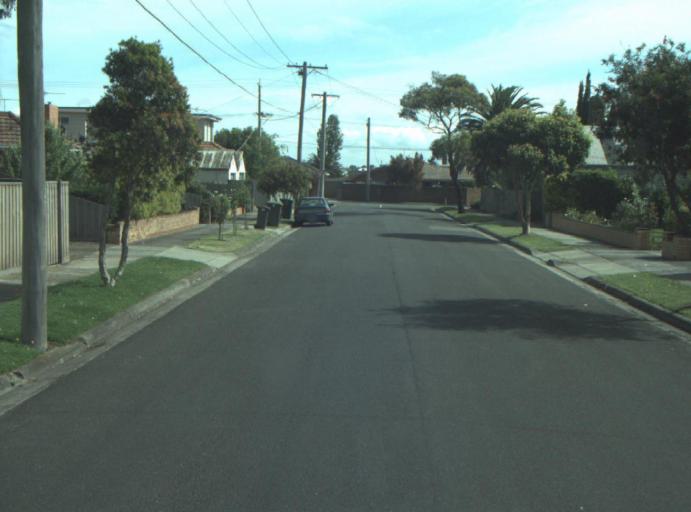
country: AU
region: Victoria
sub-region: Greater Geelong
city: Breakwater
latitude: -38.1710
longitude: 144.3385
